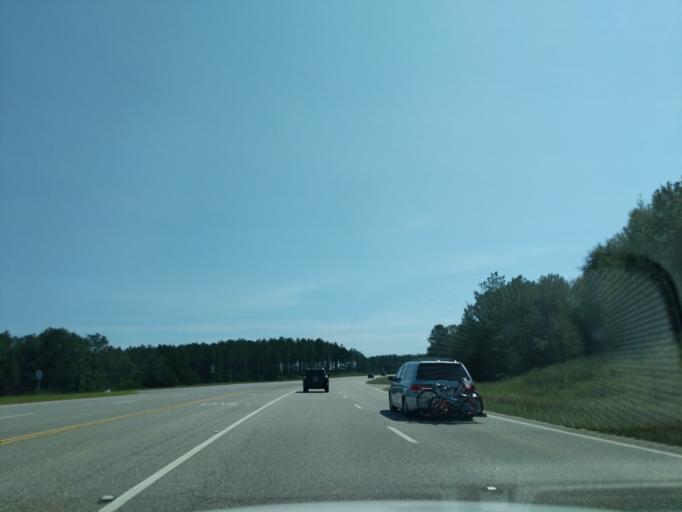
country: US
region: Alabama
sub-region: Covington County
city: Andalusia
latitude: 31.4437
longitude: -86.6143
